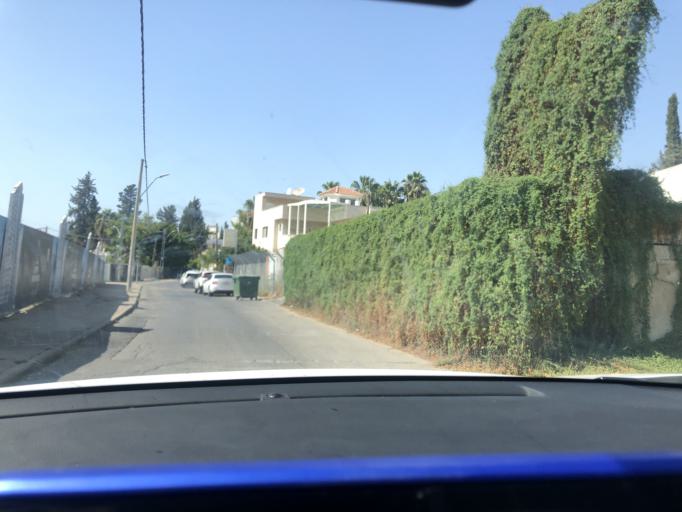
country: IL
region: Central District
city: Lod
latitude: 31.9509
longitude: 34.8929
